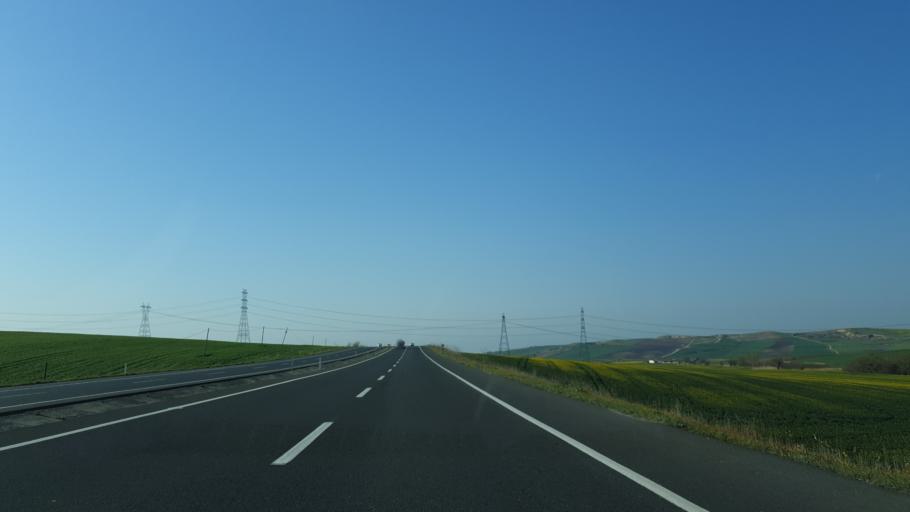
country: TR
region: Tekirdag
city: Corlu
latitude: 41.0775
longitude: 27.7414
